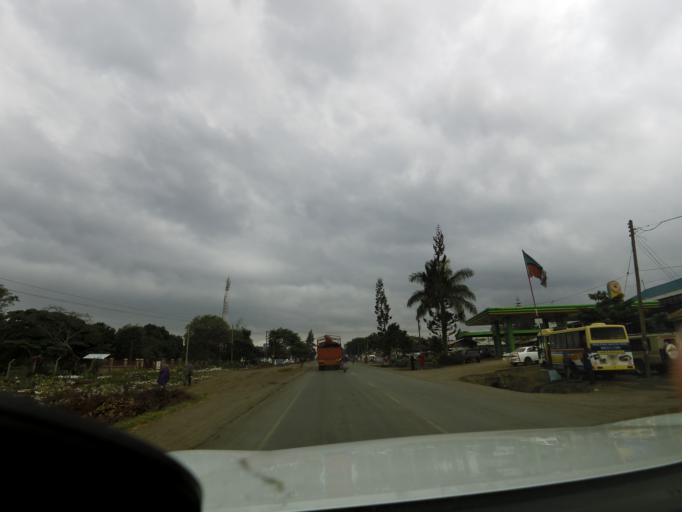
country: TZ
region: Arusha
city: Arusha
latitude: -3.3617
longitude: 36.6861
